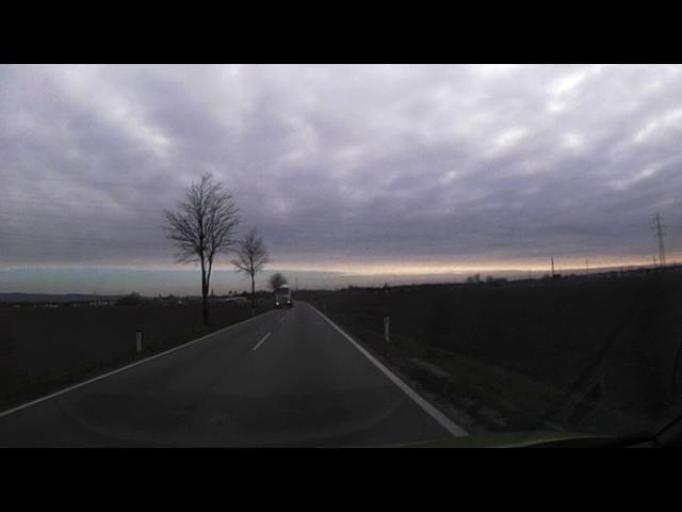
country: AT
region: Lower Austria
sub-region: Politischer Bezirk Wiener Neustadt
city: Ebenfurth
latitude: 47.8832
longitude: 16.3526
